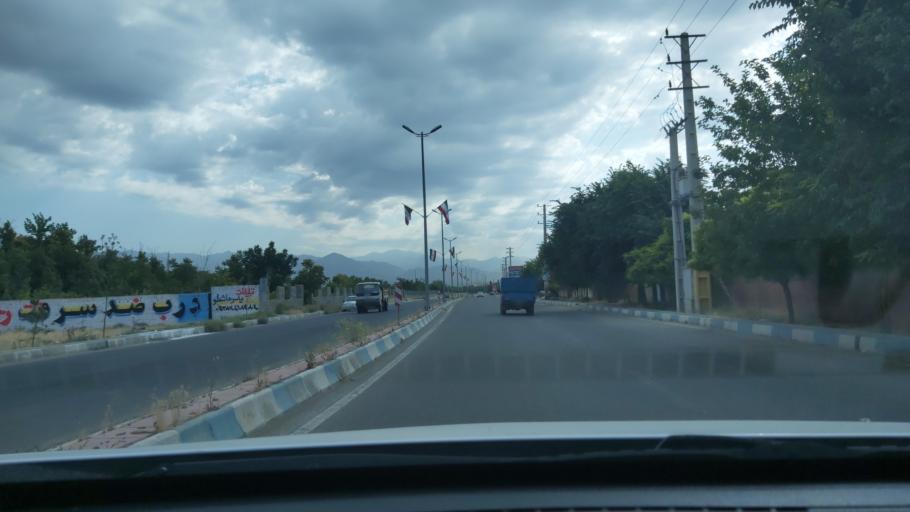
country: IR
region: Alborz
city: Hashtgerd
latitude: 35.9372
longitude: 50.7612
